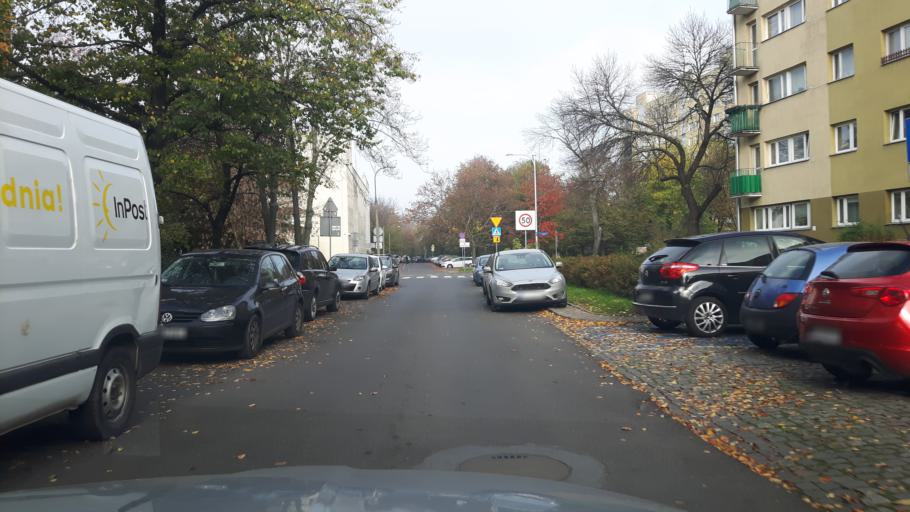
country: PL
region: Masovian Voivodeship
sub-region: Warszawa
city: Wlochy
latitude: 52.1929
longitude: 20.9718
